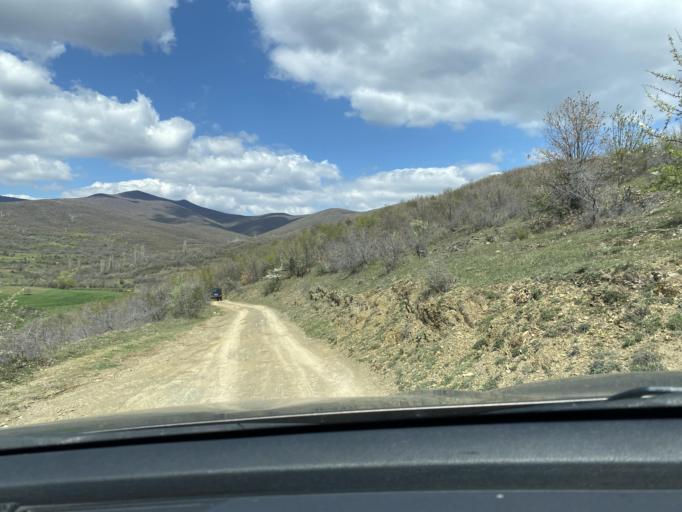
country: MK
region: Caska
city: Caska
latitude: 41.7324
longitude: 21.6516
